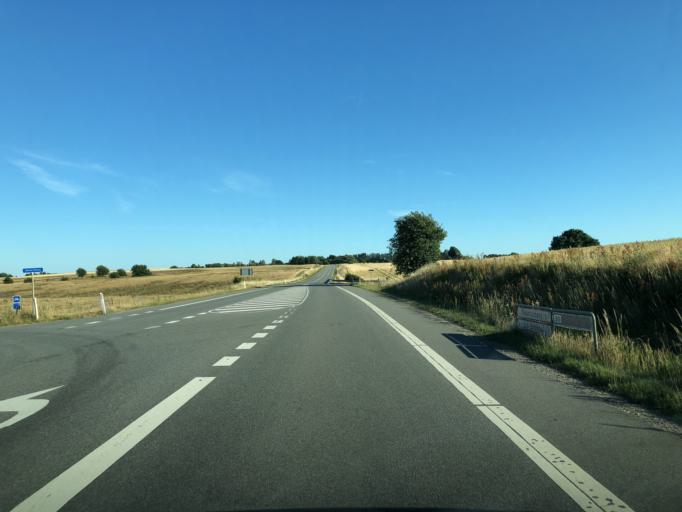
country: DK
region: Central Jutland
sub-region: Skanderborg Kommune
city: Stilling
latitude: 56.0897
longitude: 9.9702
